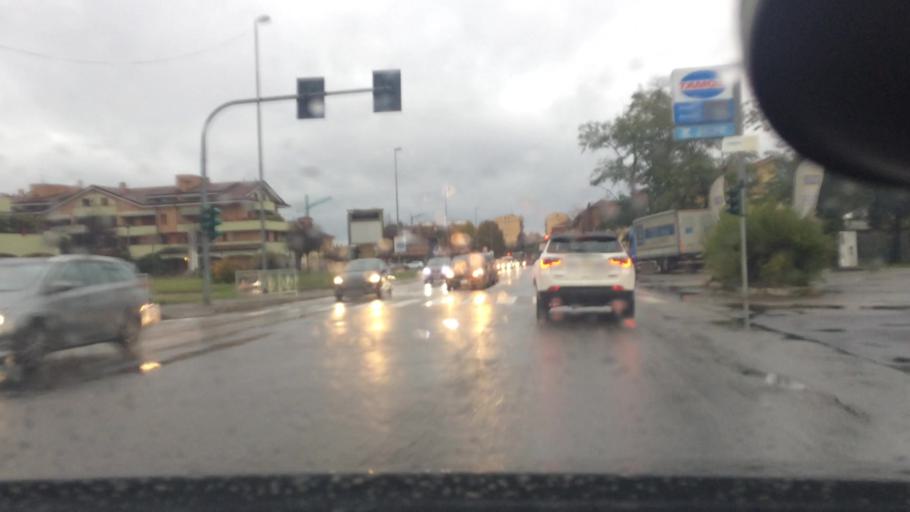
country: IT
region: Lombardy
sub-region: Citta metropolitana di Milano
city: Pogliano Milanese
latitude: 45.5448
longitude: 9.0020
